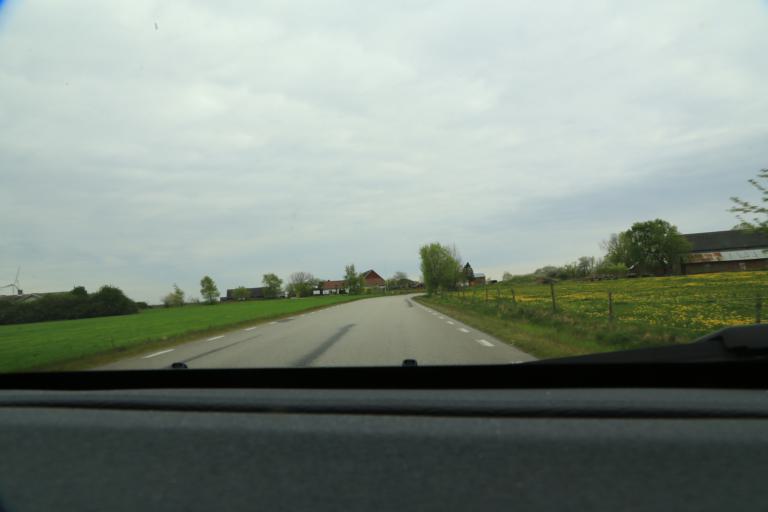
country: SE
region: Halland
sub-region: Varbergs Kommun
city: Tvaaker
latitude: 57.0441
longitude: 12.3636
